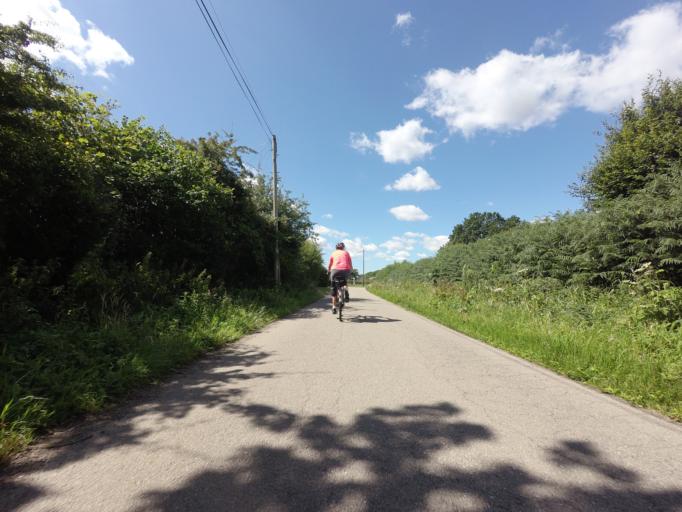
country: GB
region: England
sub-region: East Sussex
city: Horam
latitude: 50.9087
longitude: 0.1930
